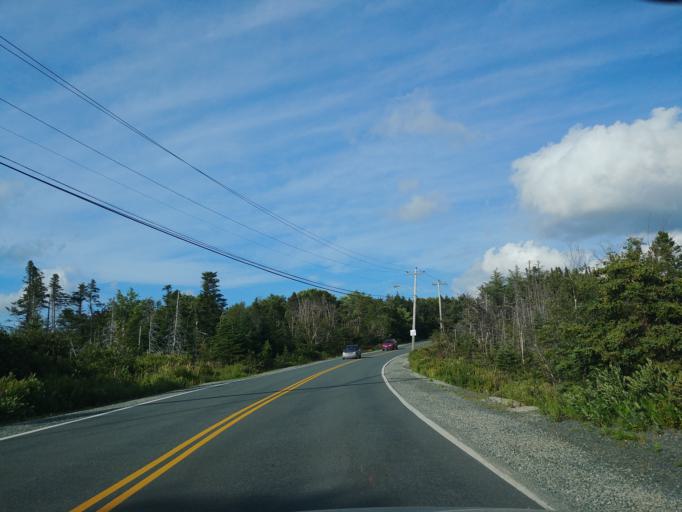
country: CA
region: Newfoundland and Labrador
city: St. John's
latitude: 47.5695
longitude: -52.7617
